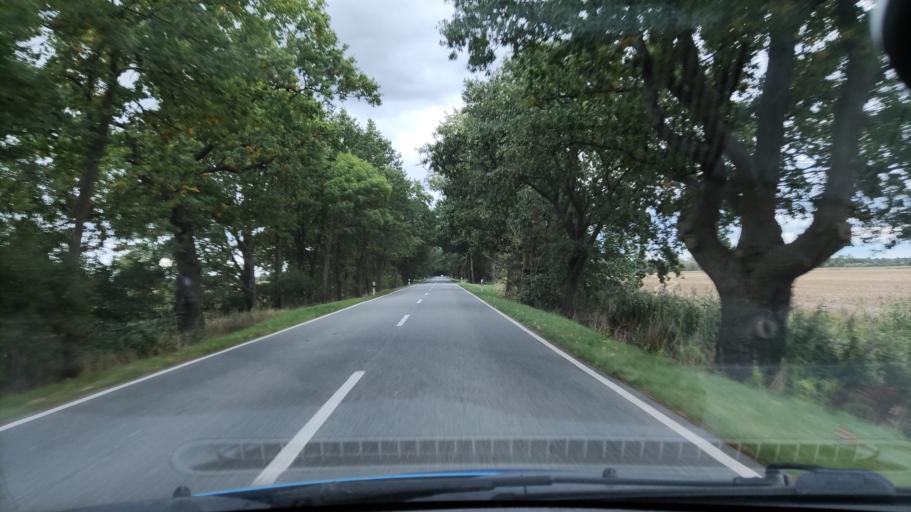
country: DE
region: Lower Saxony
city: Neu Darchau
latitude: 53.3261
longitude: 10.9491
